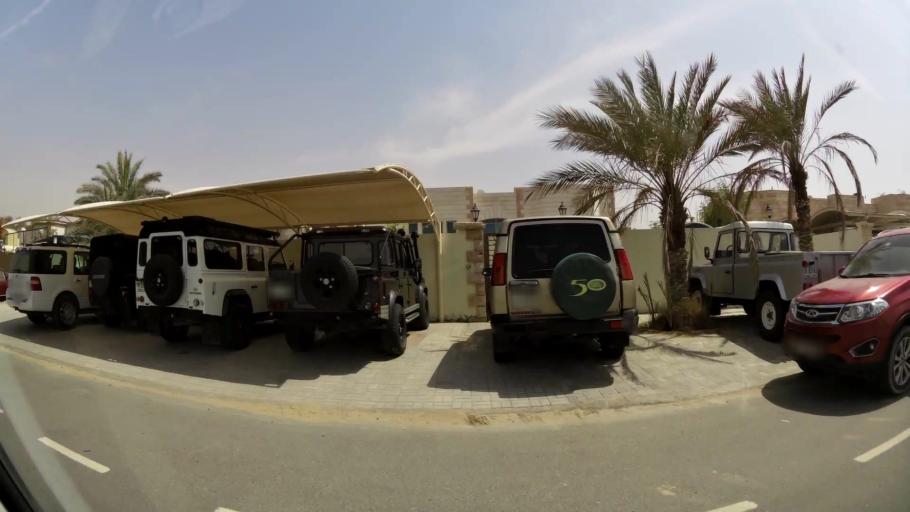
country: AE
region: Ash Shariqah
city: Sharjah
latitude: 25.2559
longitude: 55.4713
